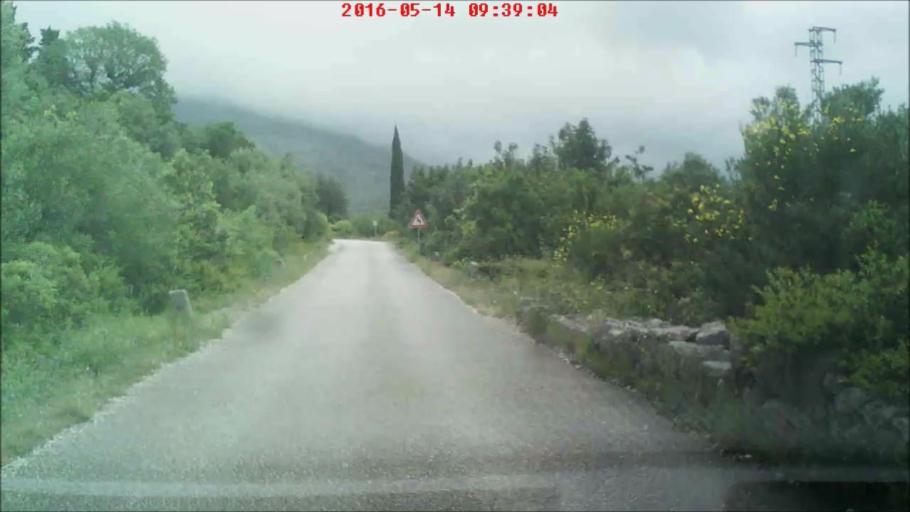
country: HR
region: Dubrovacko-Neretvanska
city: Podgora
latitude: 42.7909
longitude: 17.8894
